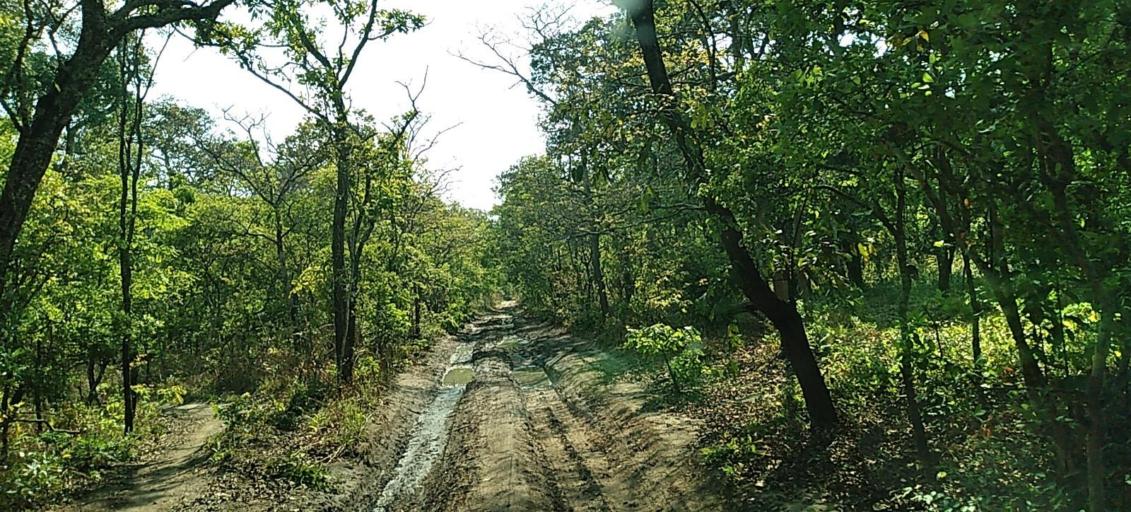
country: ZM
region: North-Western
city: Mwinilunga
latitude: -11.3024
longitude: 24.8391
